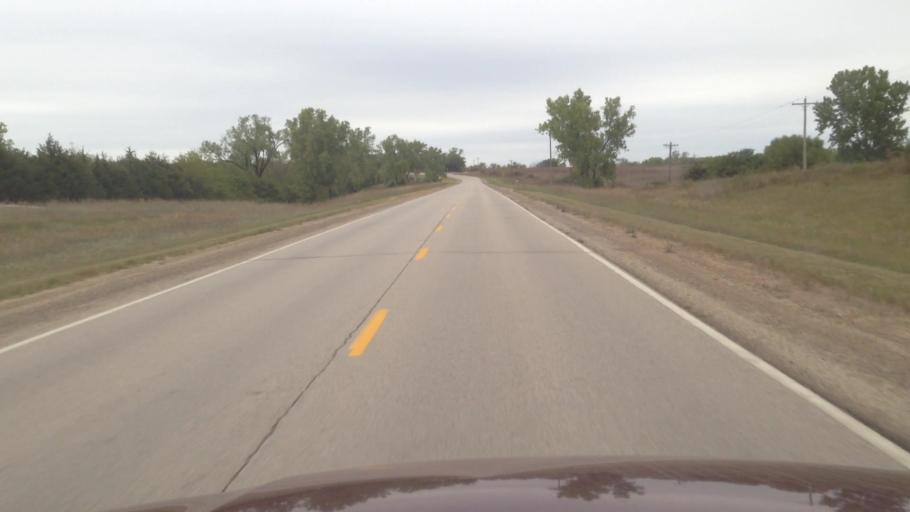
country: US
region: Kansas
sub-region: Jefferson County
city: Oskaloosa
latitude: 39.1220
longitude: -95.4836
